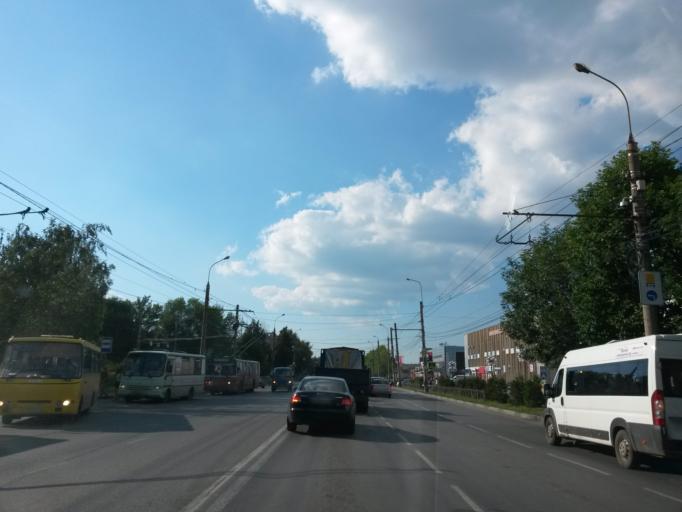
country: RU
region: Ivanovo
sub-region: Gorod Ivanovo
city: Ivanovo
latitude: 56.9649
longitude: 41.0227
